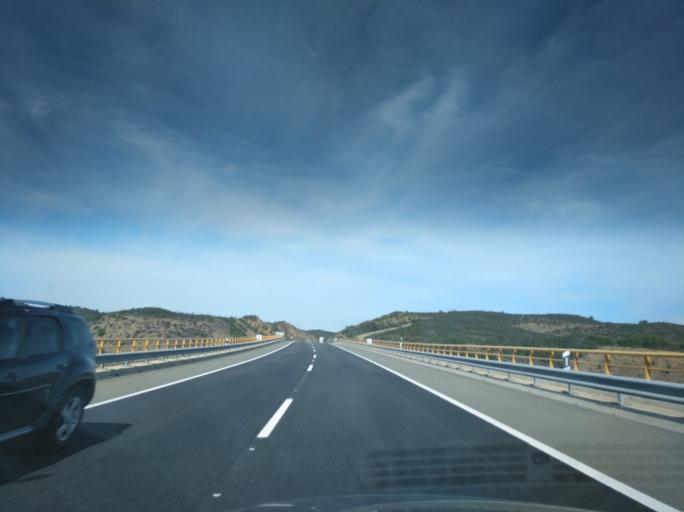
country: PT
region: Faro
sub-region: Alcoutim
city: Alcoutim
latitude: 37.3879
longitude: -7.5263
